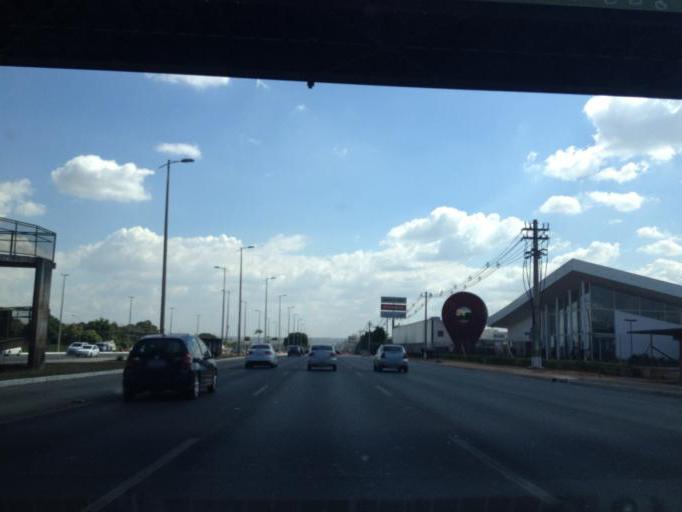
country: BR
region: Federal District
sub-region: Brasilia
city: Brasilia
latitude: -15.8086
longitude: -47.9574
